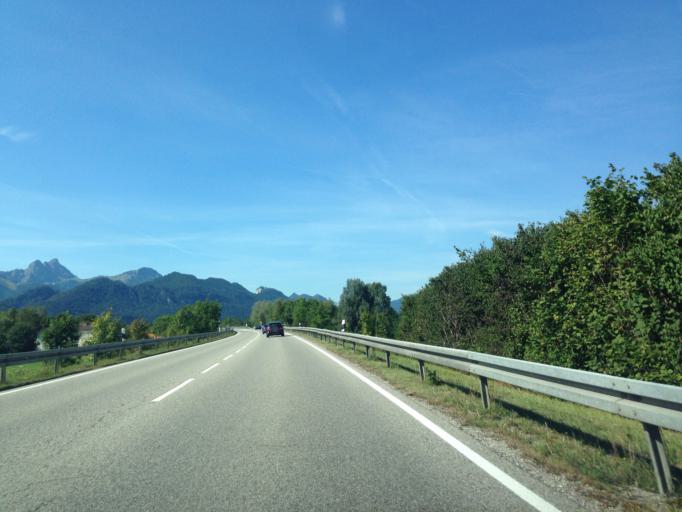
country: DE
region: Bavaria
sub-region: Swabia
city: Fuessen
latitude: 47.5803
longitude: 10.6827
